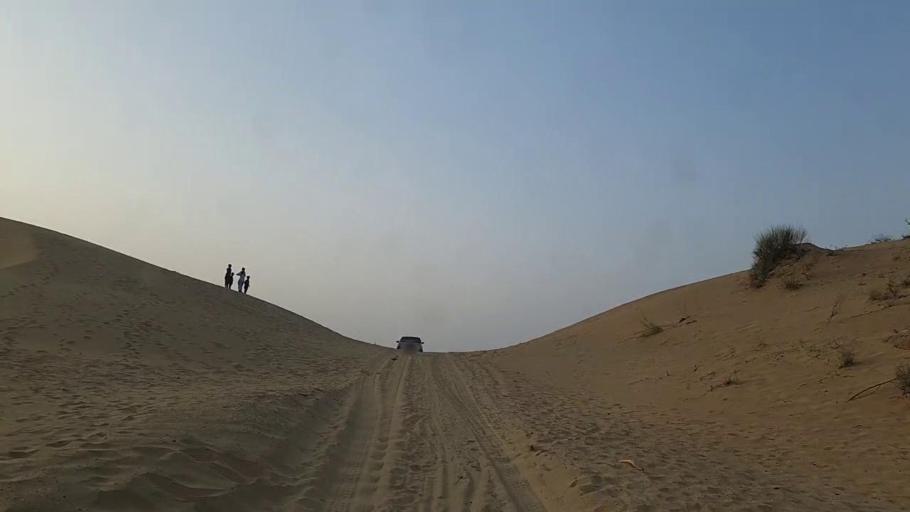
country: PK
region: Sindh
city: Naukot
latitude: 24.6825
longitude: 69.4553
